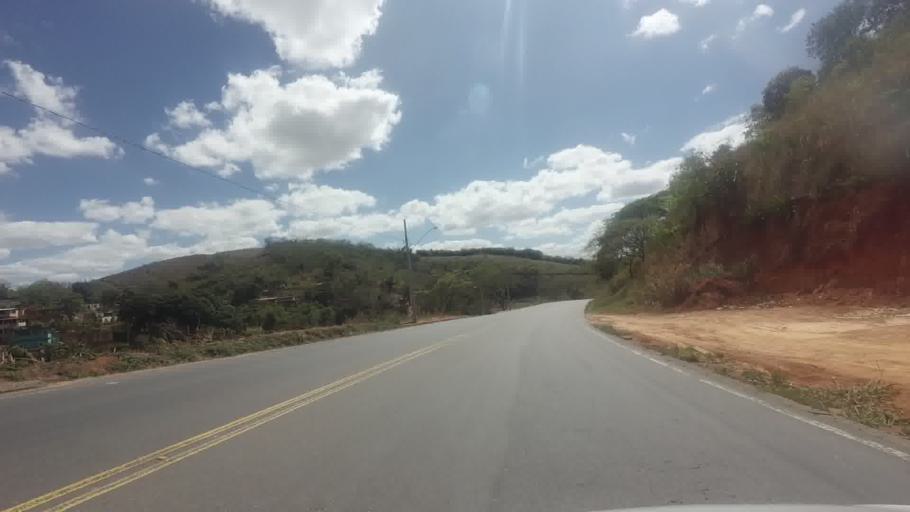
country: BR
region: Minas Gerais
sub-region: Alem Paraiba
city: Alem Paraiba
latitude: -21.8638
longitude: -42.6725
